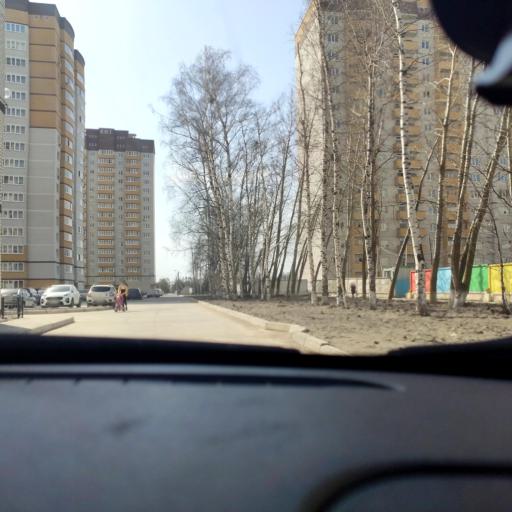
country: RU
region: Voronezj
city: Podgornoye
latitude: 51.7318
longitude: 39.1871
